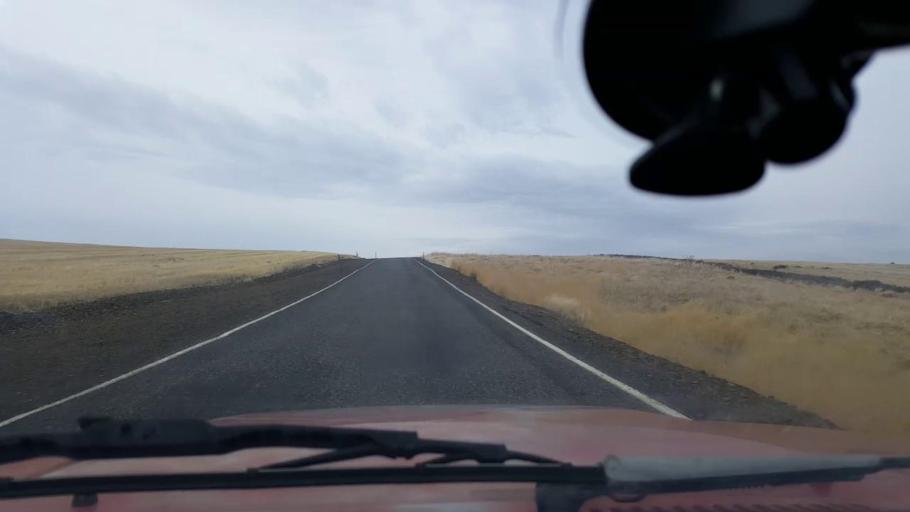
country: US
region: Washington
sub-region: Asotin County
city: Clarkston Heights-Vineland
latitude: 46.3447
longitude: -117.2521
